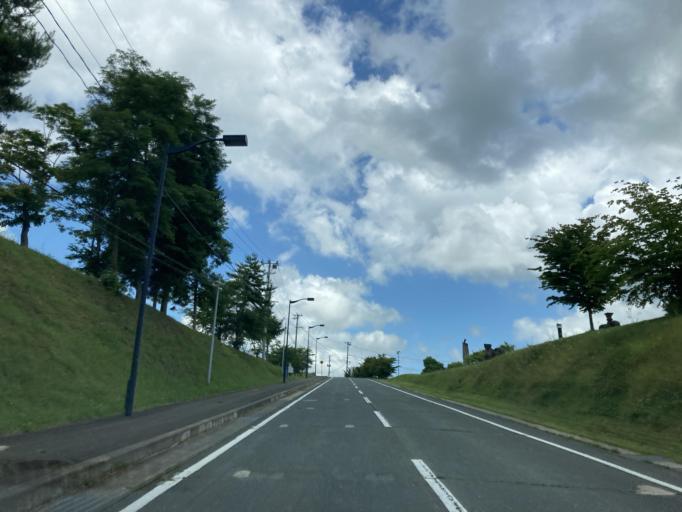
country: JP
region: Iwate
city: Ichinohe
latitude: 39.9707
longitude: 141.2127
